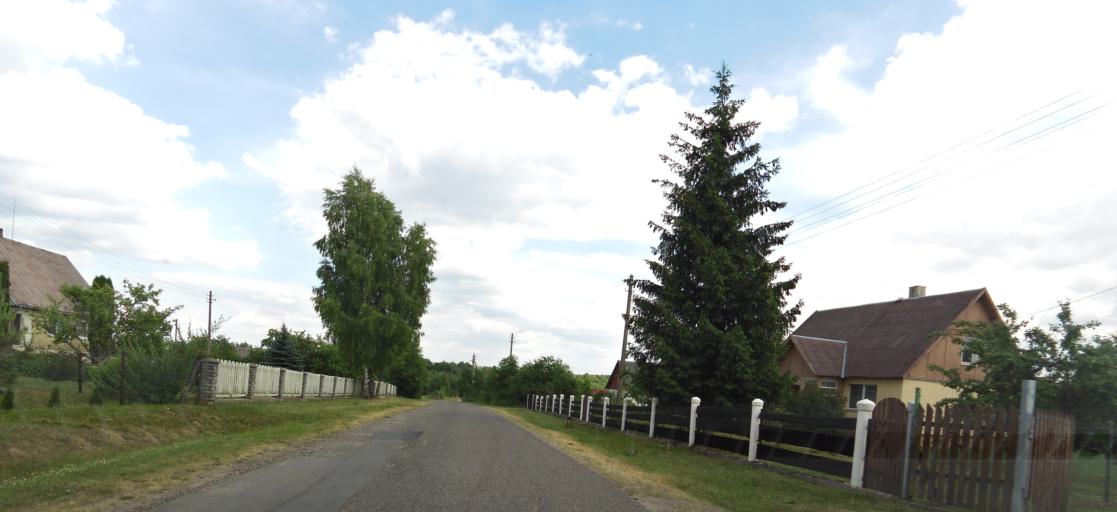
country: LT
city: Skaidiskes
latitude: 54.5325
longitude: 25.6468
